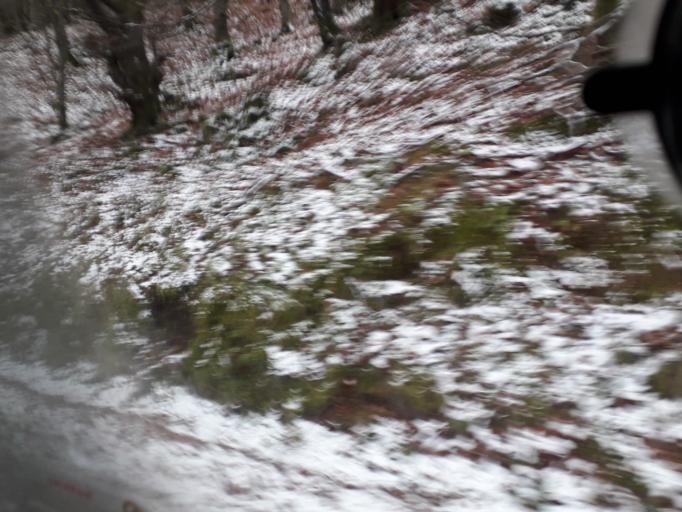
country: IE
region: Leinster
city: Ballyboden
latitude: 53.2434
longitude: -6.3017
